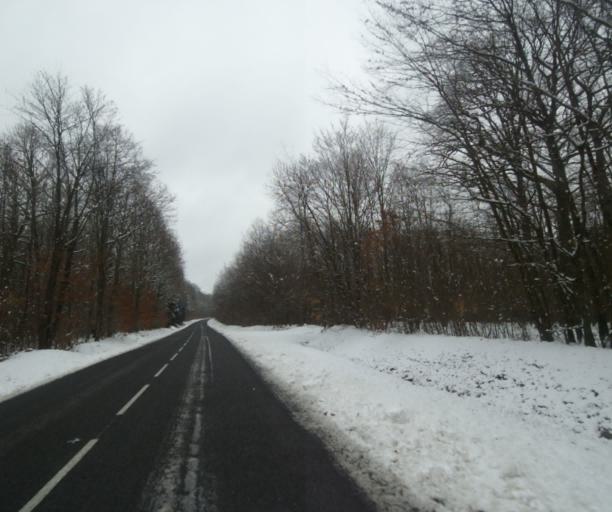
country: FR
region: Champagne-Ardenne
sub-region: Departement de la Haute-Marne
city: Laneuville-a-Remy
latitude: 48.4464
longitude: 4.8630
